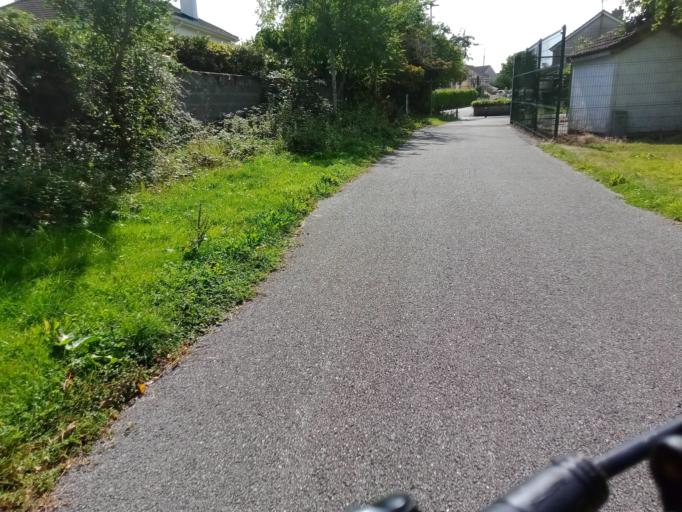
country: IE
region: Munster
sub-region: Waterford
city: Dungarvan
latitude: 52.0949
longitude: -7.6016
